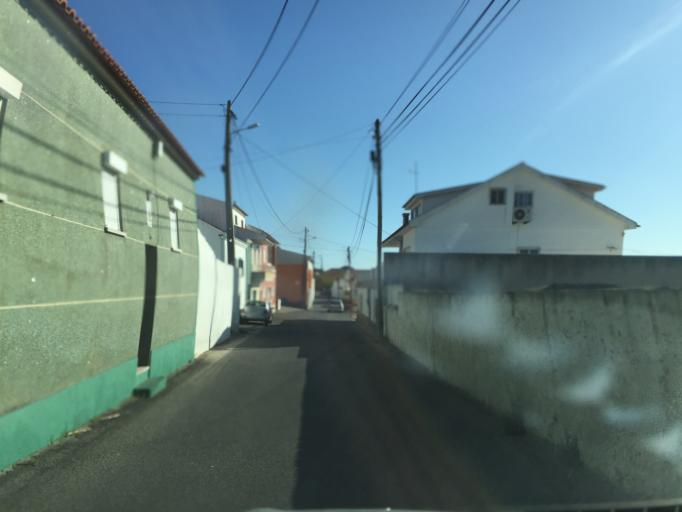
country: PT
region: Lisbon
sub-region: Torres Vedras
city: Torres Vedras
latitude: 39.0905
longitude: -9.2765
